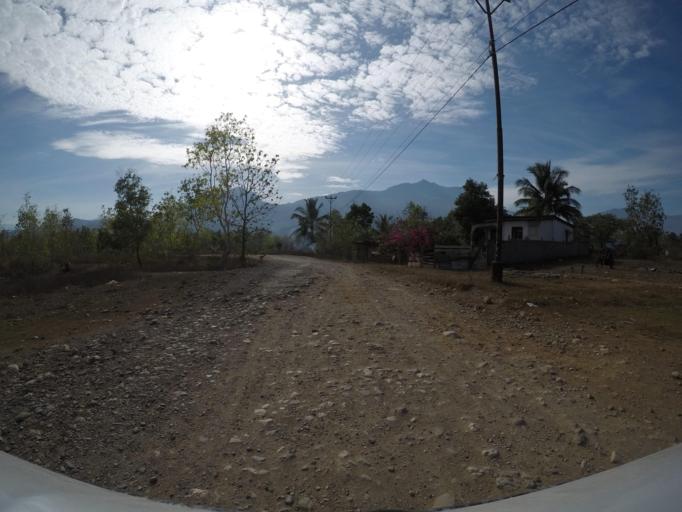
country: TL
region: Bobonaro
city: Maliana
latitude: -8.9268
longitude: 125.2050
